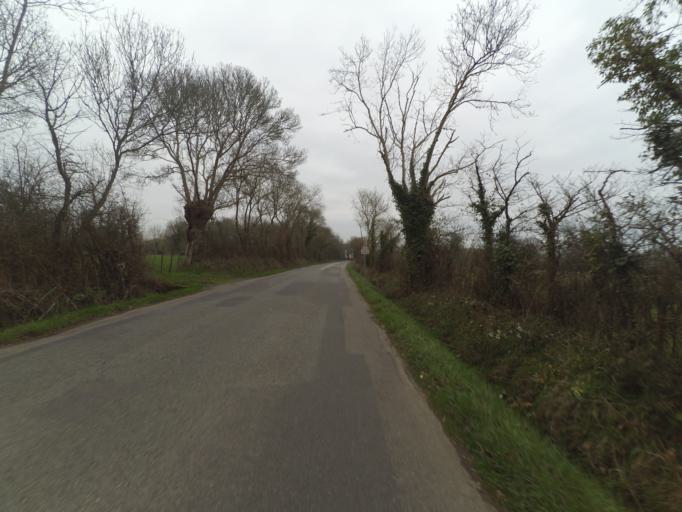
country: FR
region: Pays de la Loire
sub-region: Departement de la Loire-Atlantique
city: Indre
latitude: 47.2276
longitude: -1.6837
